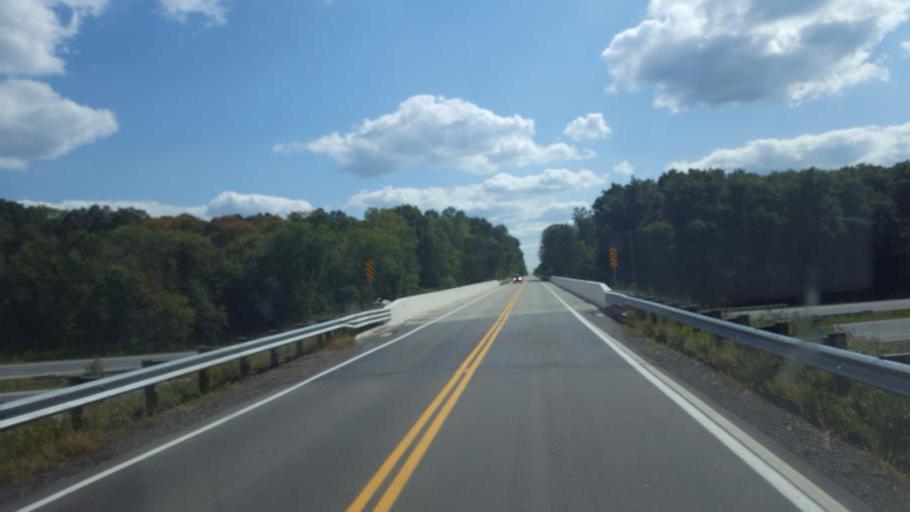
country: US
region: Ohio
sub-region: Ashland County
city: Ashland
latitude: 40.8764
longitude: -82.2115
